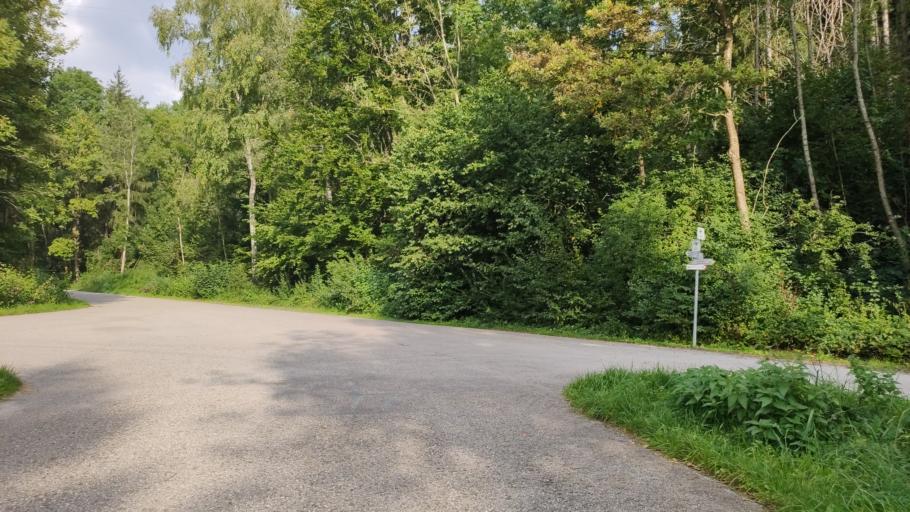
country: DE
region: Bavaria
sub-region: Upper Bavaria
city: Scheuring
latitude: 48.1473
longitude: 10.8694
